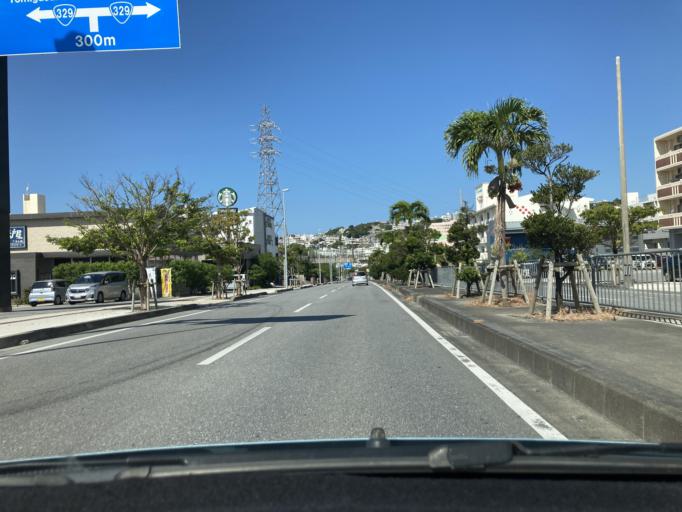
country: JP
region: Okinawa
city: Tomigusuku
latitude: 26.1937
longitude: 127.7127
